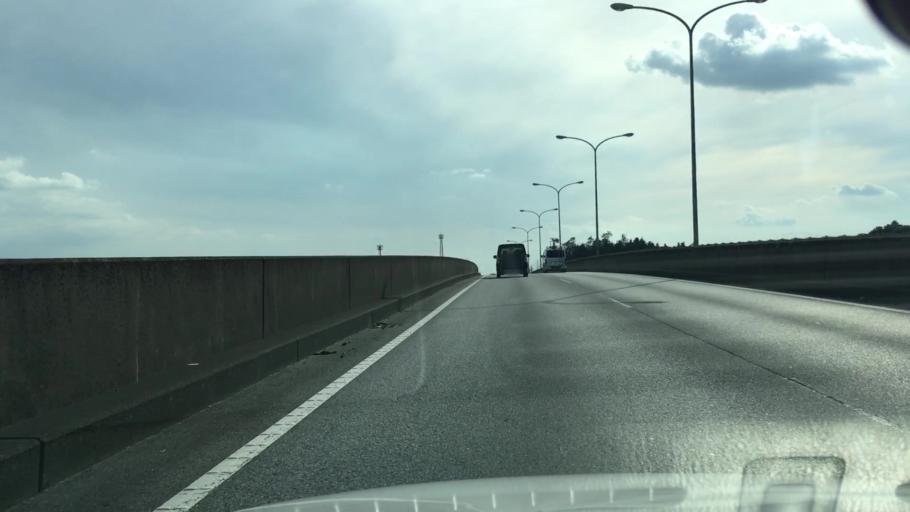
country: JP
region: Tochigi
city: Utsunomiya-shi
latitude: 36.5375
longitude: 139.9320
